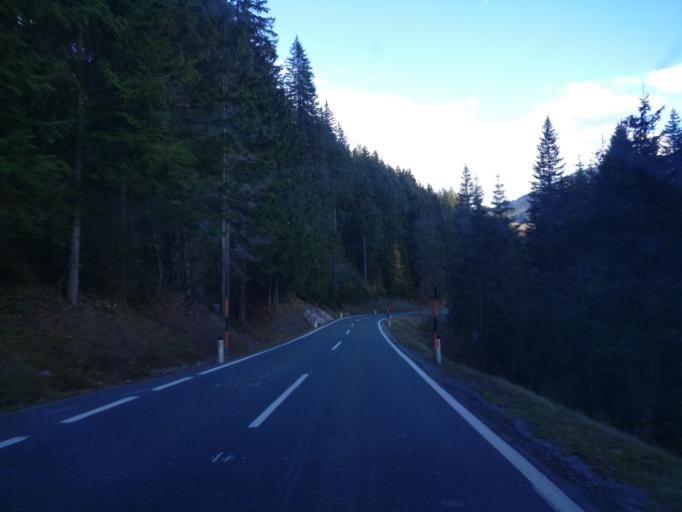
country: AT
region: Salzburg
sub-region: Politischer Bezirk Zell am See
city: Dienten am Hochkonig
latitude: 47.3969
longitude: 13.0049
